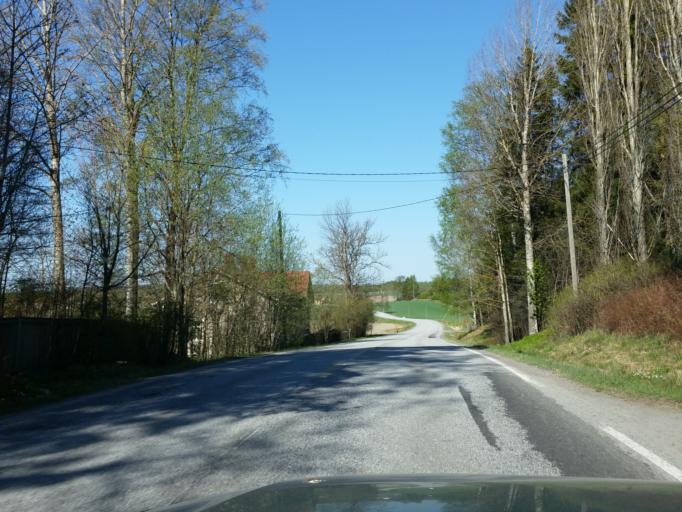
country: FI
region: Uusimaa
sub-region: Helsinki
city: Lohja
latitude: 60.1762
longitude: 24.0901
